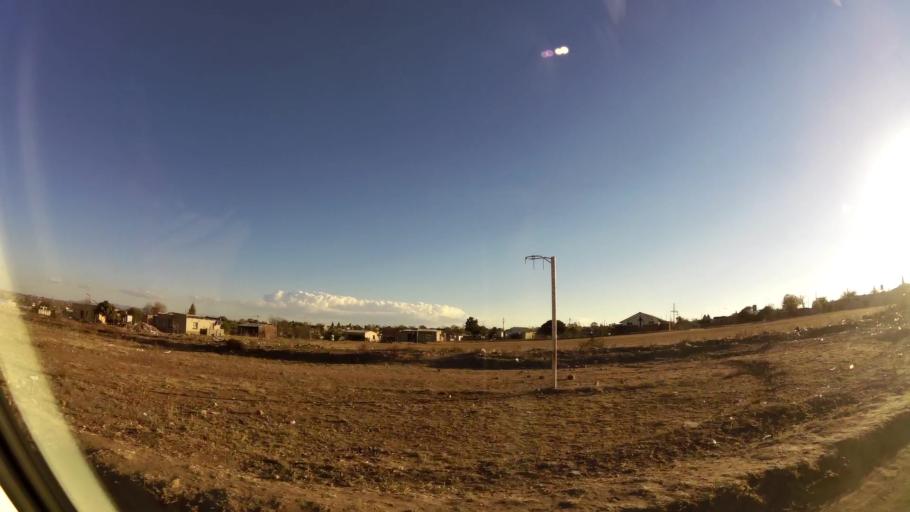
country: ZA
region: Limpopo
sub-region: Capricorn District Municipality
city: Polokwane
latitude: -23.8146
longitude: 29.3801
